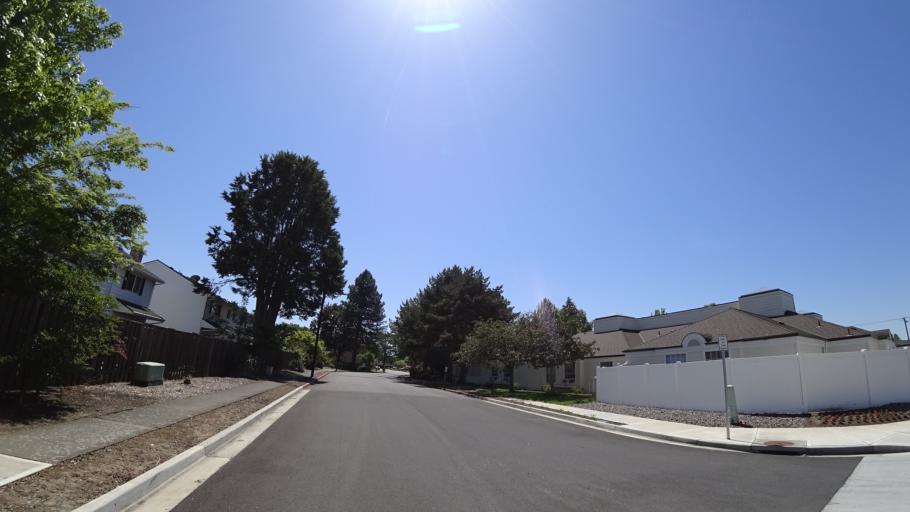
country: US
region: Oregon
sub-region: Washington County
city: Beaverton
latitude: 45.4860
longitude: -122.8240
